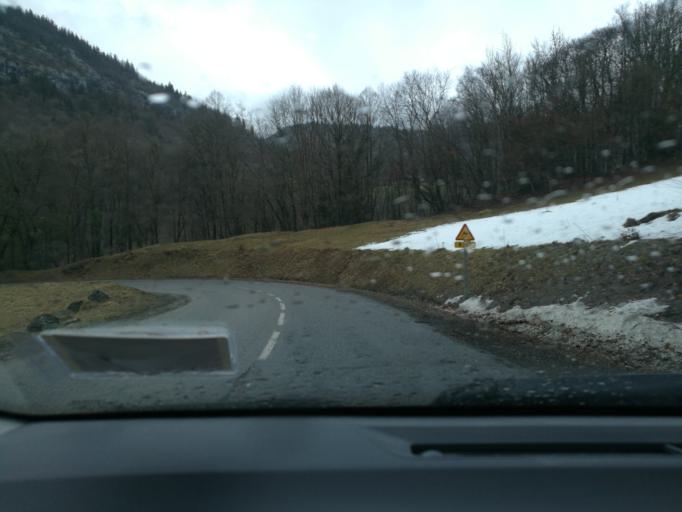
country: FR
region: Rhone-Alpes
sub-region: Departement de la Haute-Savoie
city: Araches-la-Frasse
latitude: 46.0468
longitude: 6.6178
